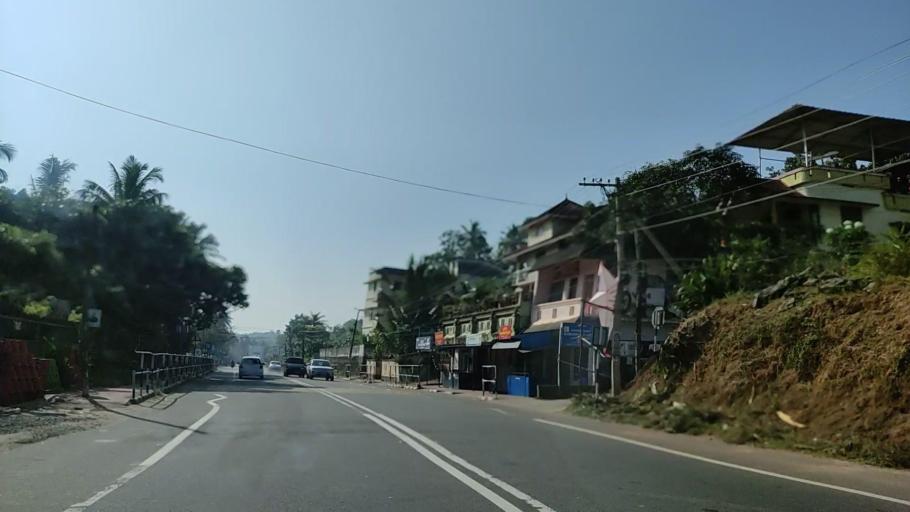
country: IN
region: Kerala
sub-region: Kollam
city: Punalur
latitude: 8.9293
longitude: 76.8536
